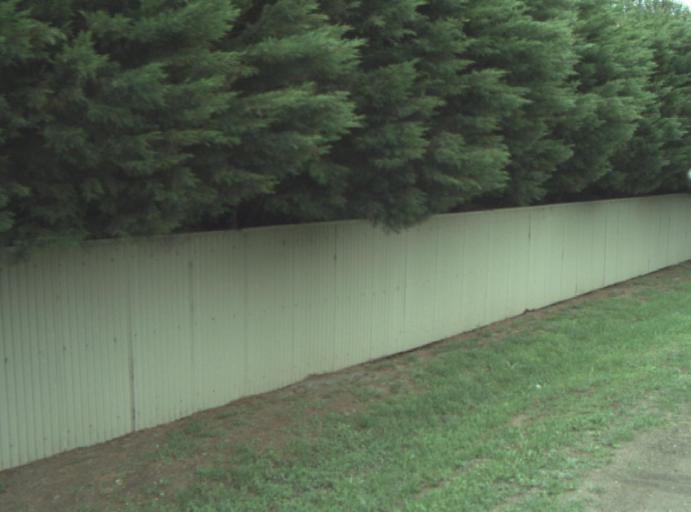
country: AU
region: Victoria
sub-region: Greater Geelong
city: Bell Post Hill
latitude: -38.0727
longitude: 144.3284
